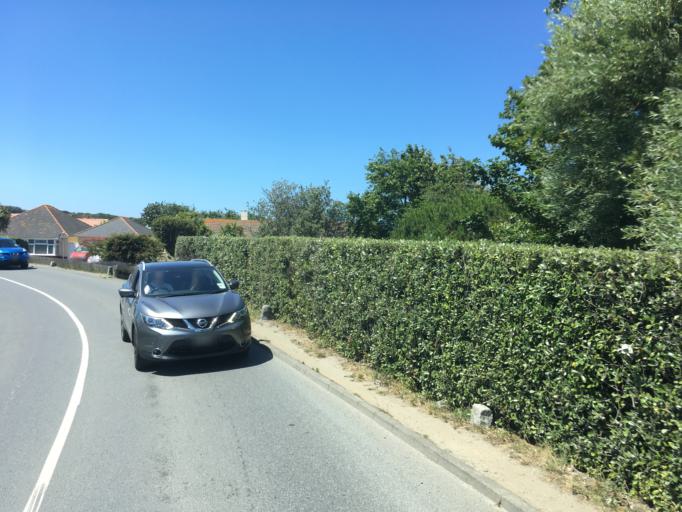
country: GG
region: St Peter Port
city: Saint Peter Port
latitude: 49.4950
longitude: -2.5551
